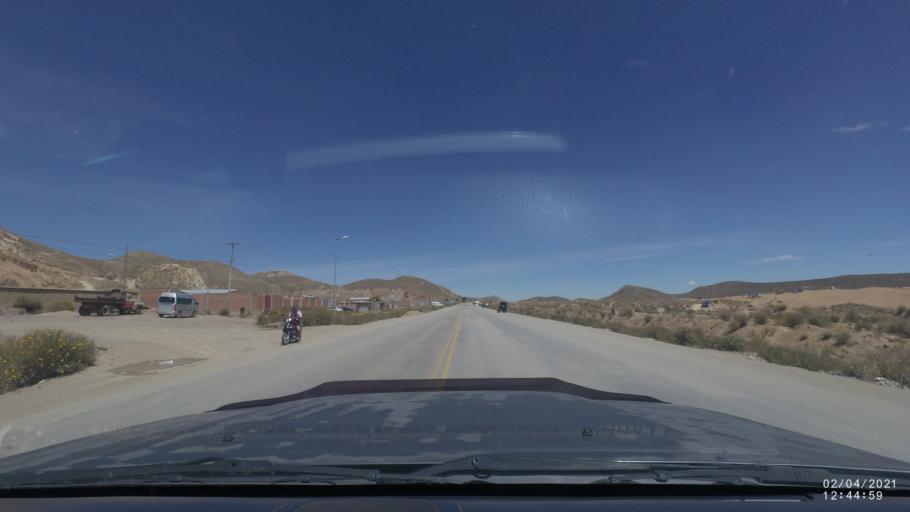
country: BO
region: Oruro
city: Oruro
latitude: -17.9312
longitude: -67.1312
